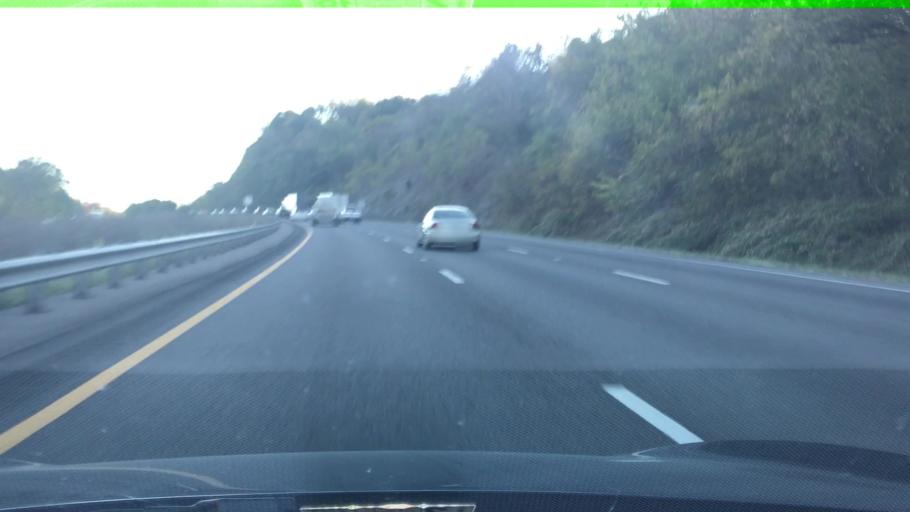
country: US
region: Virginia
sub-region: Montgomery County
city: Shawsville
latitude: 37.2051
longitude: -80.2657
